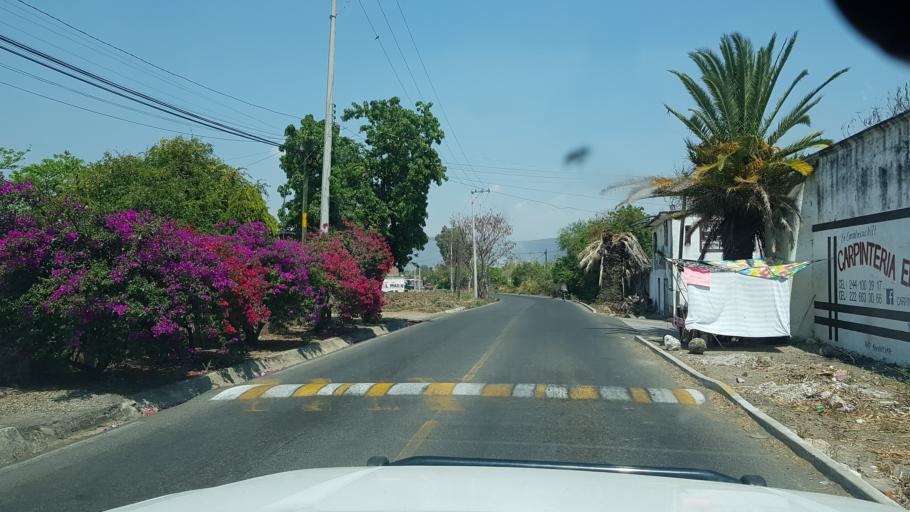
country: MX
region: Puebla
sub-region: Huaquechula
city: Cacaloxuchitl
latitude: 18.7891
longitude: -98.4709
